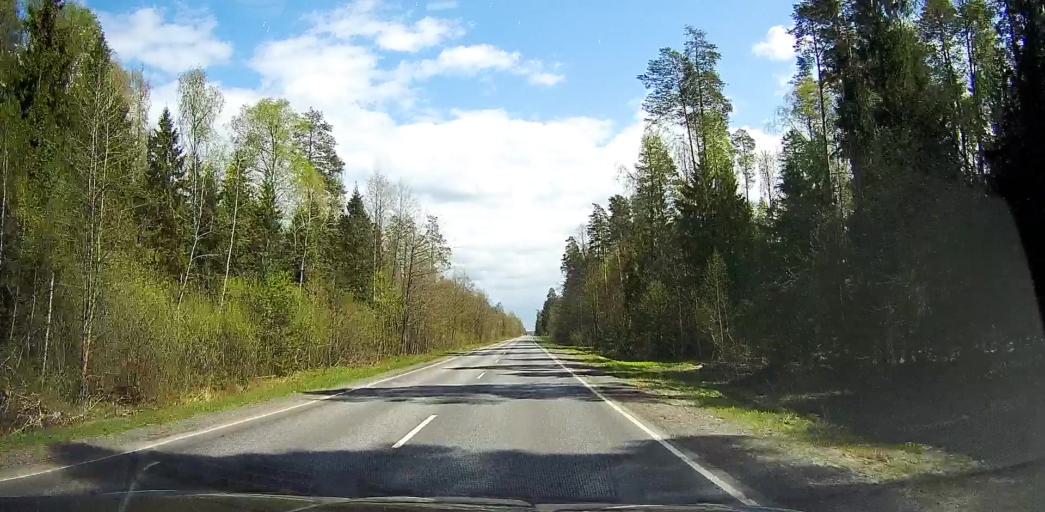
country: RU
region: Moskovskaya
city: Davydovo
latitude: 55.5514
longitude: 38.7675
